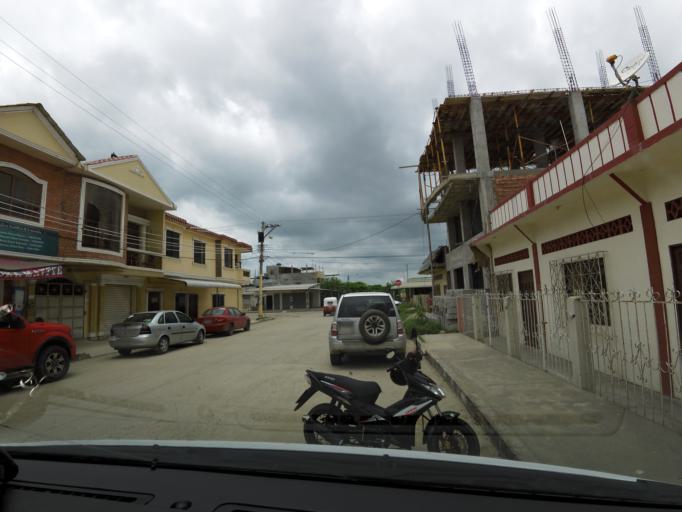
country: EC
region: El Oro
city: Huaquillas
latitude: -3.4825
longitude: -80.2348
